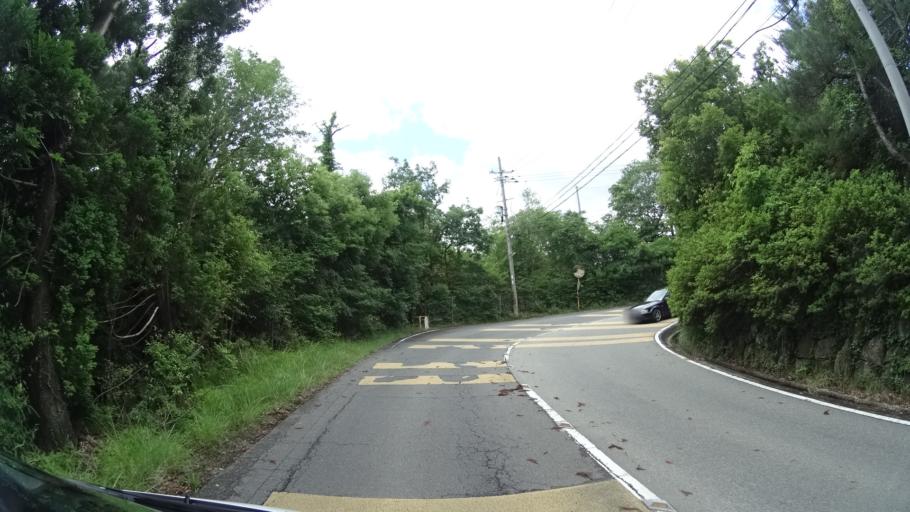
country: JP
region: Kyoto
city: Kameoka
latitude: 35.0098
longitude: 135.4607
